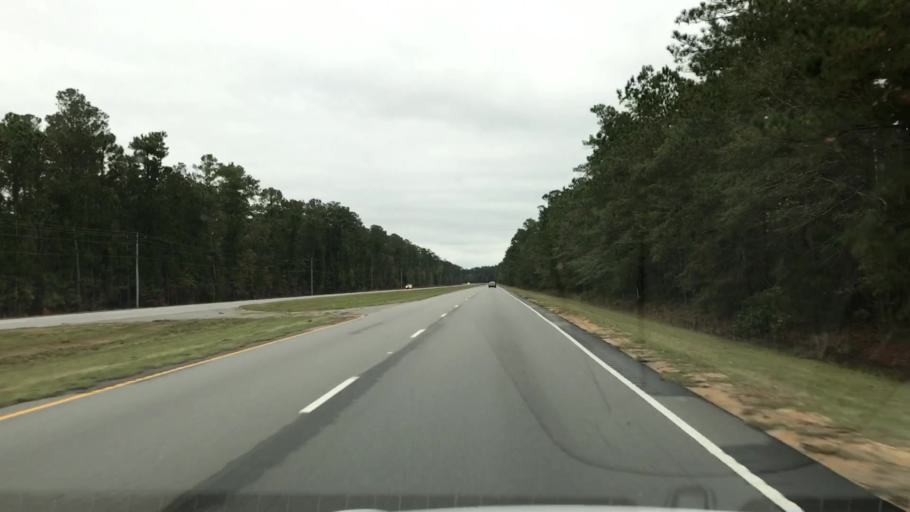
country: US
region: South Carolina
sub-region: Georgetown County
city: Georgetown
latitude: 33.2655
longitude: -79.3614
